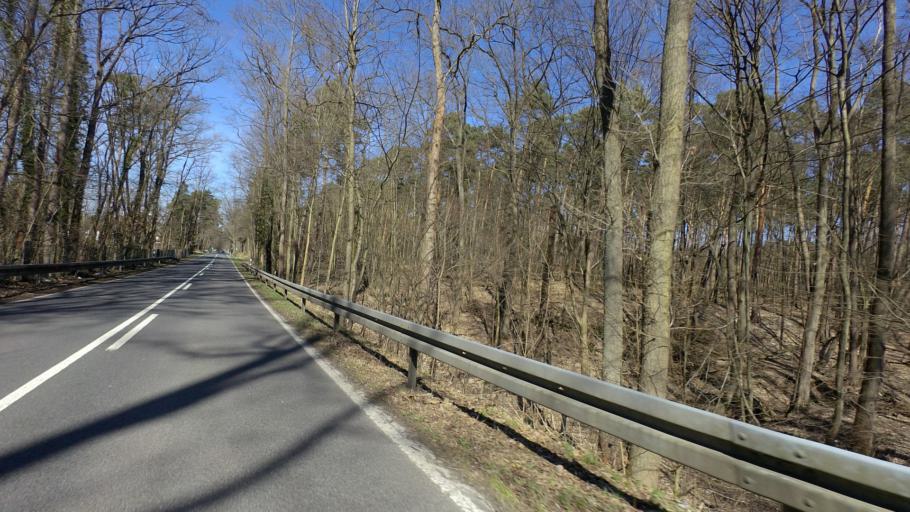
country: DE
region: Brandenburg
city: Bad Saarow
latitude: 52.2584
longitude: 14.0750
